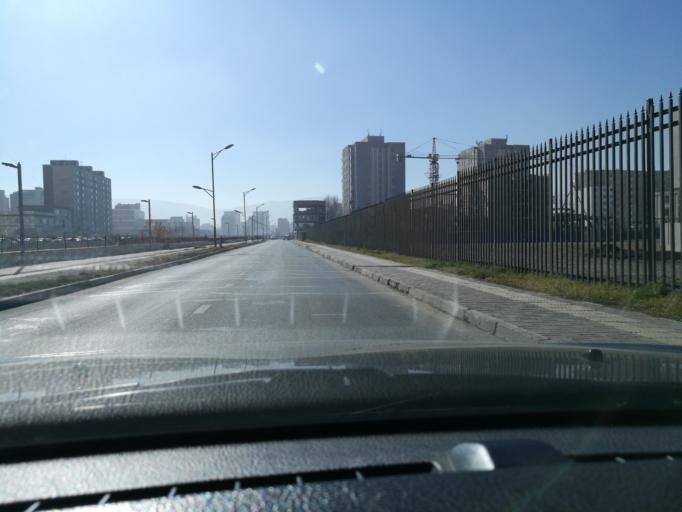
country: MN
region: Ulaanbaatar
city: Ulaanbaatar
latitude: 47.9282
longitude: 106.9314
